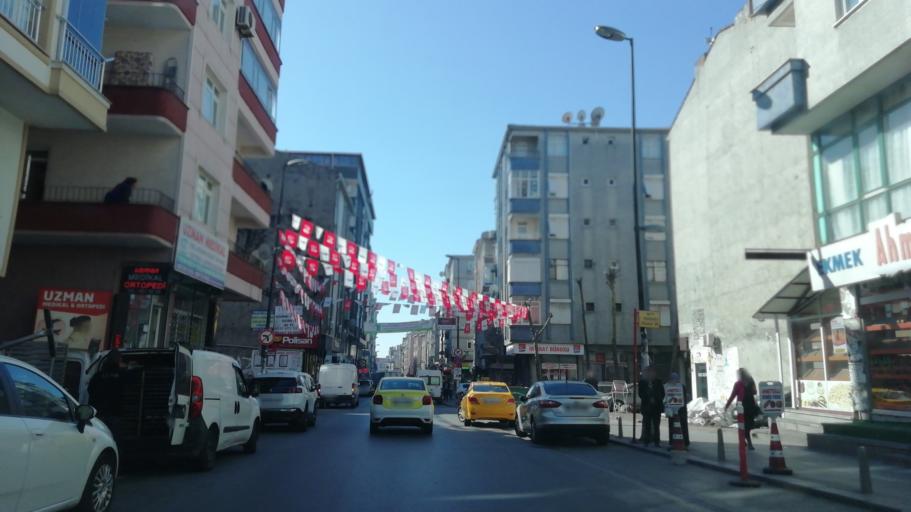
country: TR
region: Istanbul
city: Bahcelievler
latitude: 40.9988
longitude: 28.8386
